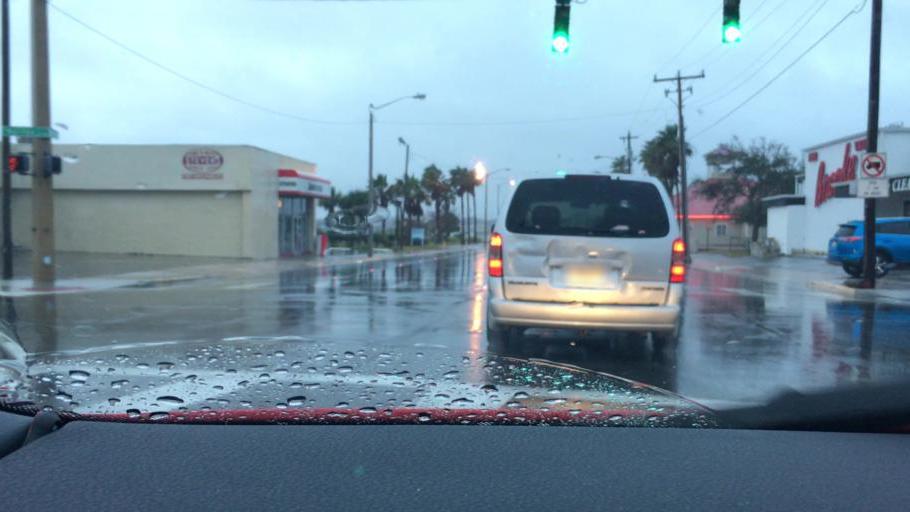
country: US
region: Florida
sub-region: Volusia County
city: Daytona Beach
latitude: 29.2248
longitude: -81.0135
